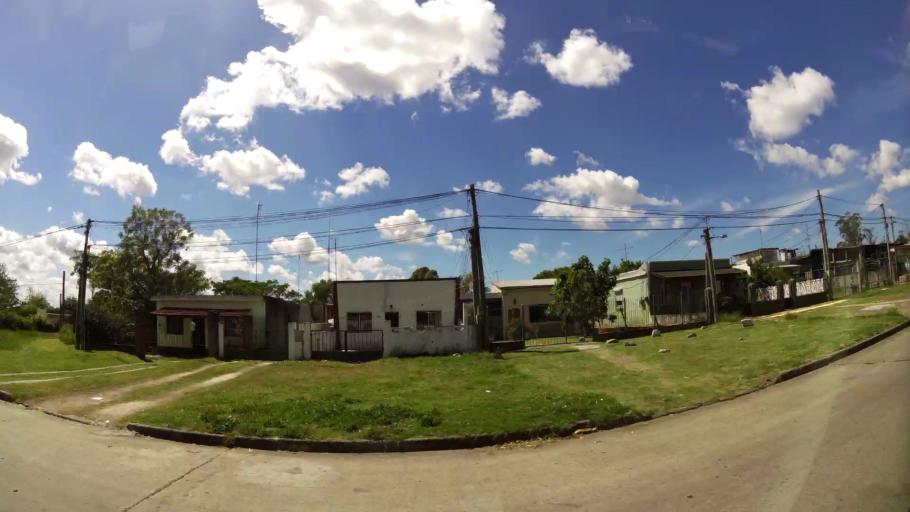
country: UY
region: Canelones
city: Paso de Carrasco
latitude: -34.8374
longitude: -56.1315
